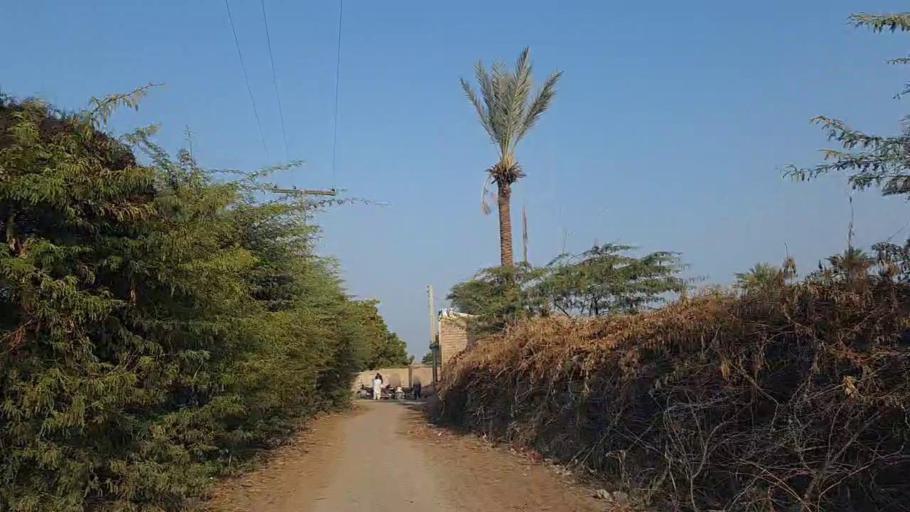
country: PK
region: Sindh
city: Jam Sahib
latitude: 26.2305
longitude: 68.5996
